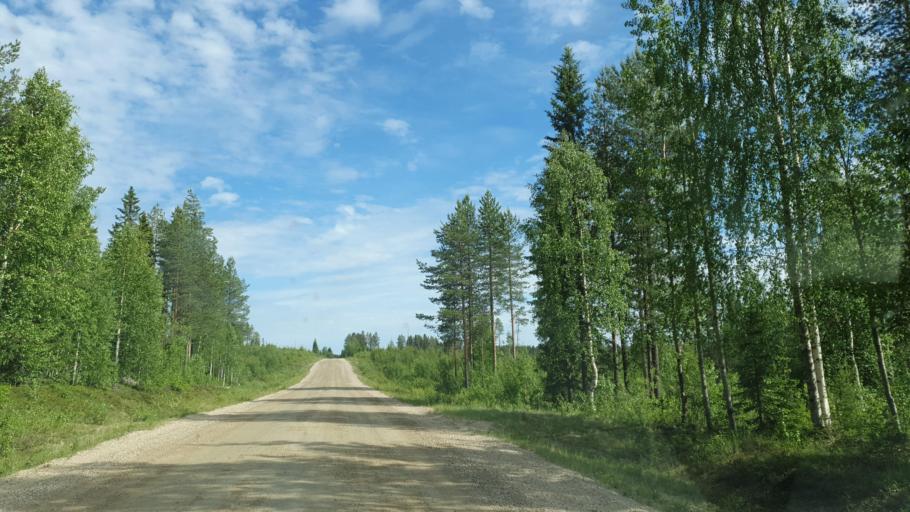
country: FI
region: Kainuu
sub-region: Kehys-Kainuu
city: Kuhmo
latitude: 64.5117
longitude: 29.4585
